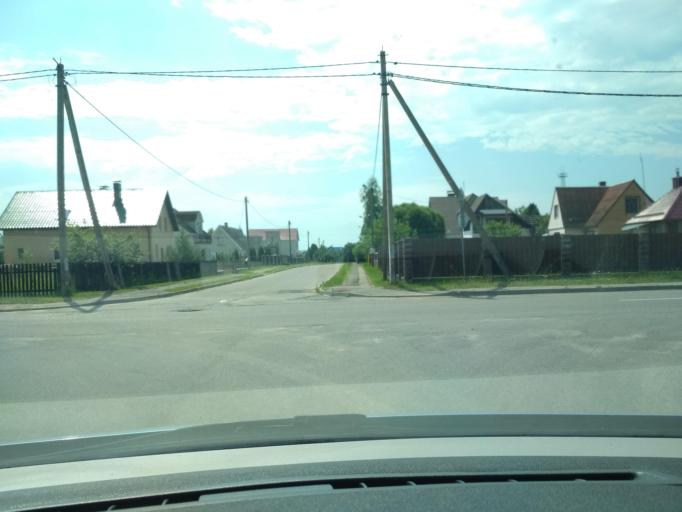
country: BY
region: Grodnenskaya
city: Astravyets
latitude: 54.6224
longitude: 25.9560
